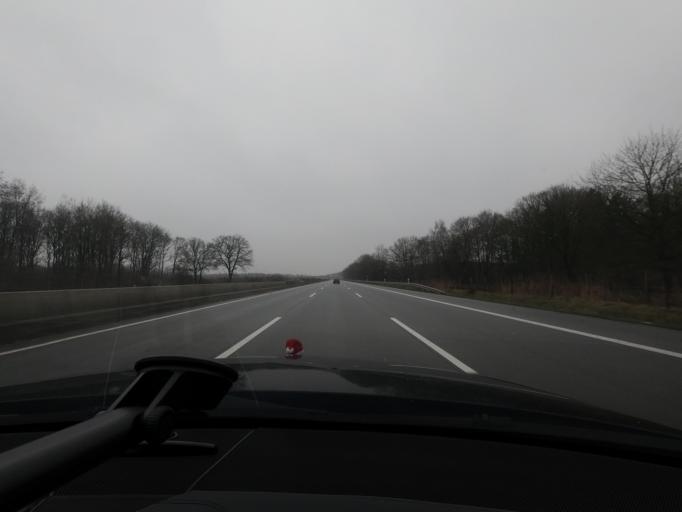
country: DE
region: Schleswig-Holstein
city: Padenstedt
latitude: 54.0231
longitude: 9.9322
